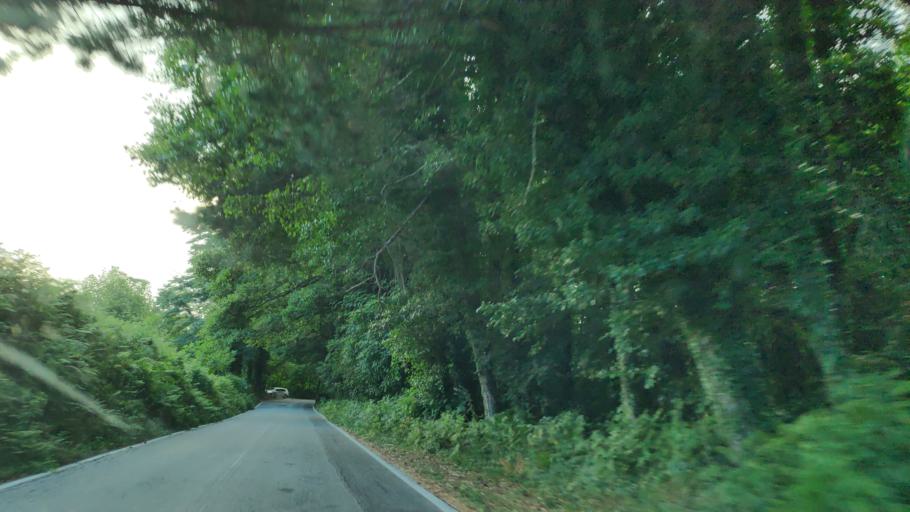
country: IT
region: Calabria
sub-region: Provincia di Vibo-Valentia
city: Mongiana
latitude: 38.5359
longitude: 16.3256
